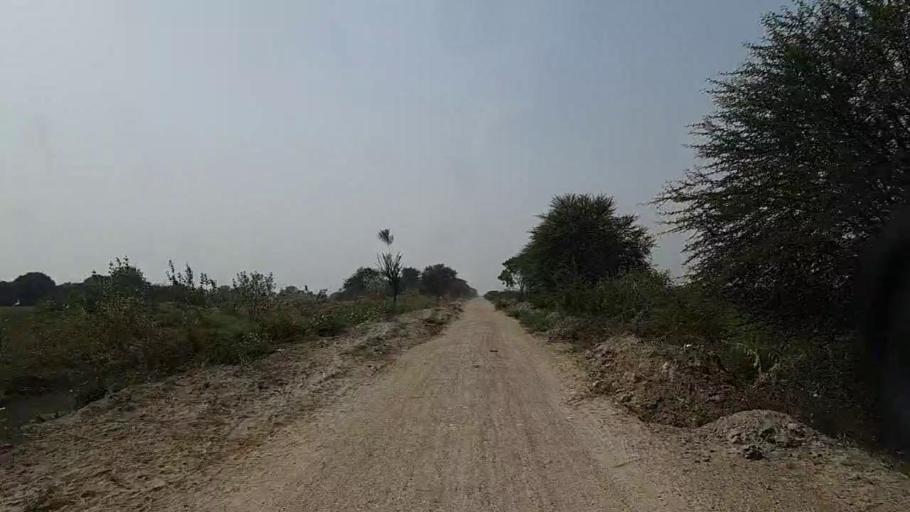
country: PK
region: Sindh
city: Naukot
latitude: 24.7700
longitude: 69.3394
